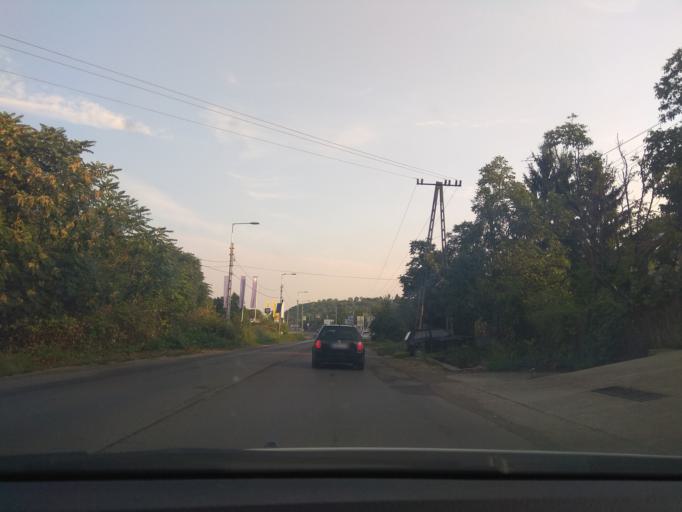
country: HU
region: Heves
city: Andornaktalya
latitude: 47.8668
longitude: 20.4057
